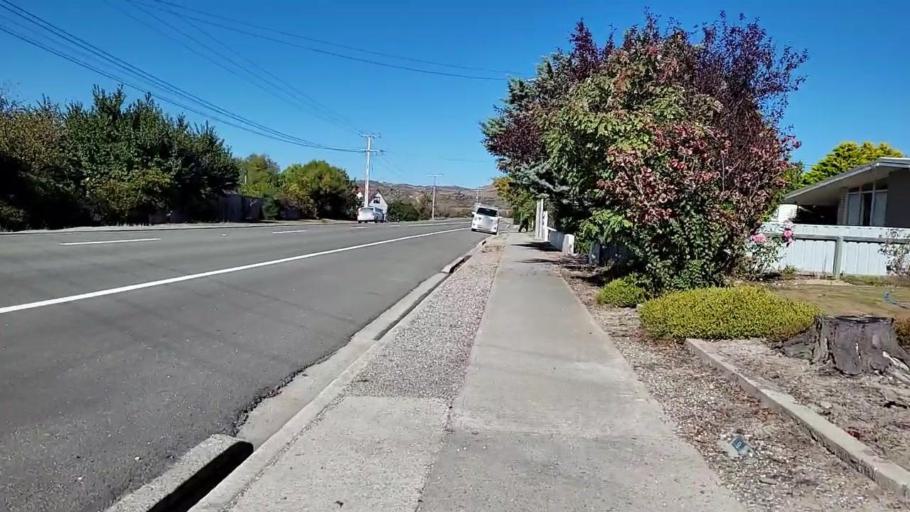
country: NZ
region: Otago
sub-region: Queenstown-Lakes District
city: Wanaka
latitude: -45.1033
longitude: 169.5953
